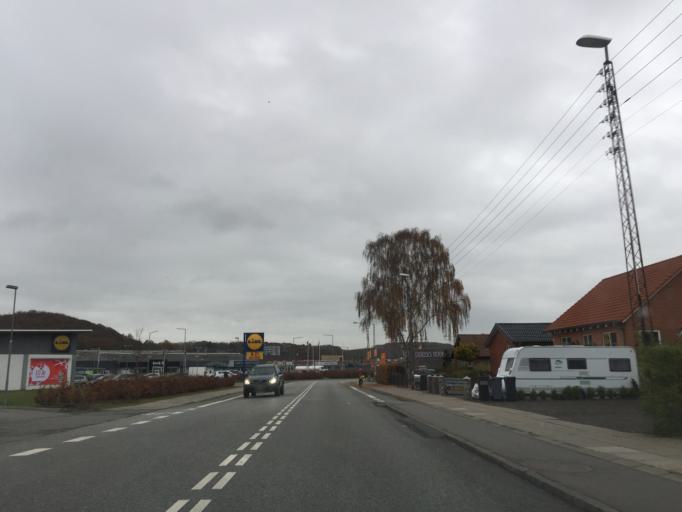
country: DK
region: Central Jutland
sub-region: Silkeborg Kommune
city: Silkeborg
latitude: 56.1852
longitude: 9.5471
